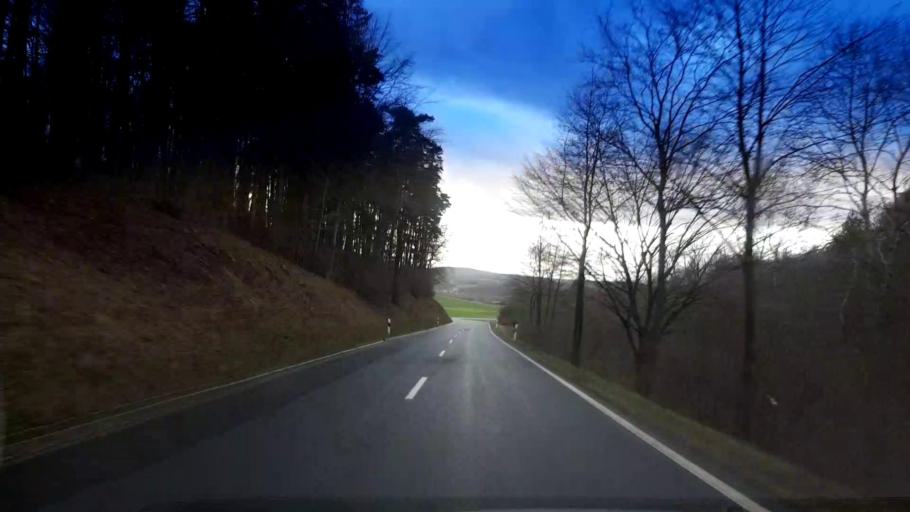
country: DE
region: Bavaria
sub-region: Regierungsbezirk Unterfranken
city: Stettfeld
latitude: 49.9686
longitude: 10.7532
